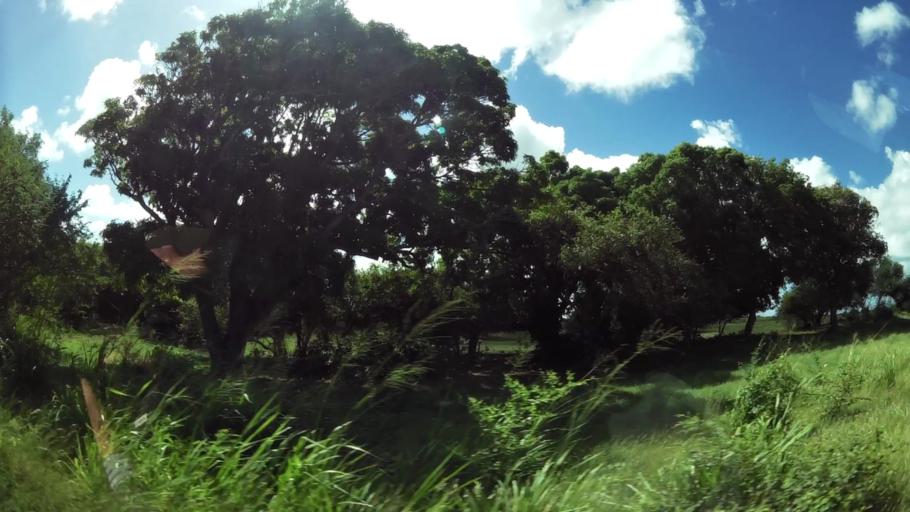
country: GP
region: Guadeloupe
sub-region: Guadeloupe
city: Anse-Bertrand
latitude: 16.4666
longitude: -61.4936
